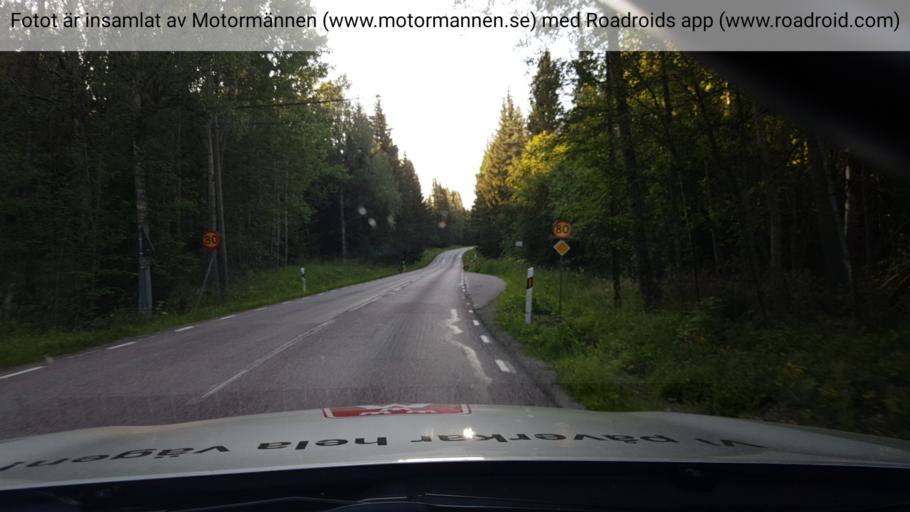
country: SE
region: Vaestmanland
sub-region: Norbergs Kommun
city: Norberg
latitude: 60.0148
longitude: 16.0373
